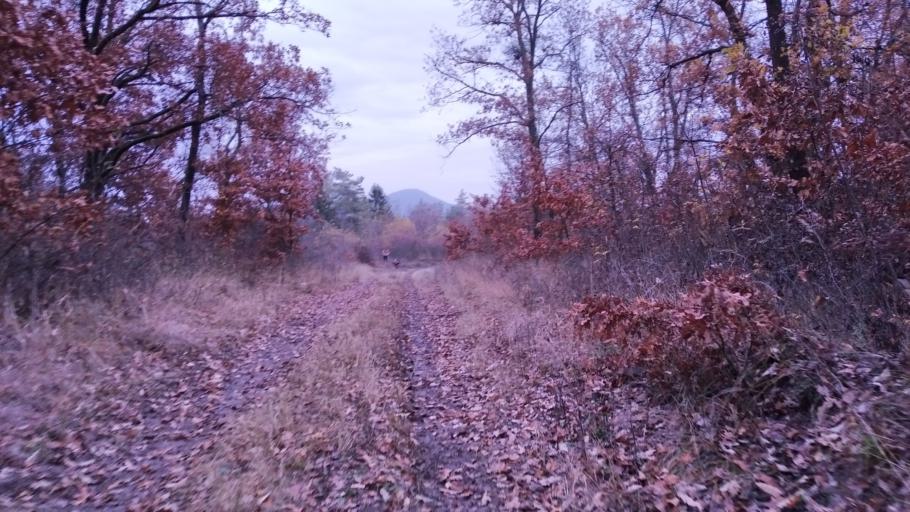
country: HU
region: Pest
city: Csobanka
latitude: 47.6698
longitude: 18.9595
